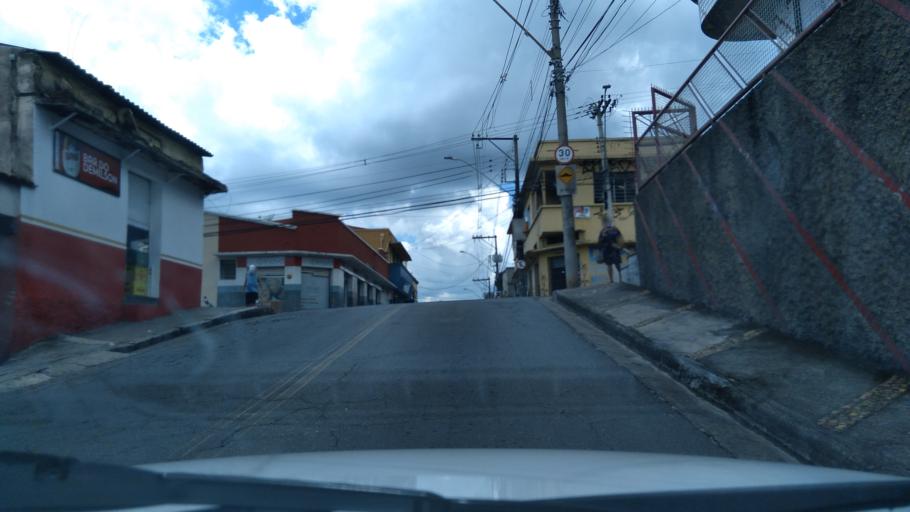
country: BR
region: Minas Gerais
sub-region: Belo Horizonte
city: Belo Horizonte
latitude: -19.9109
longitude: -43.8972
